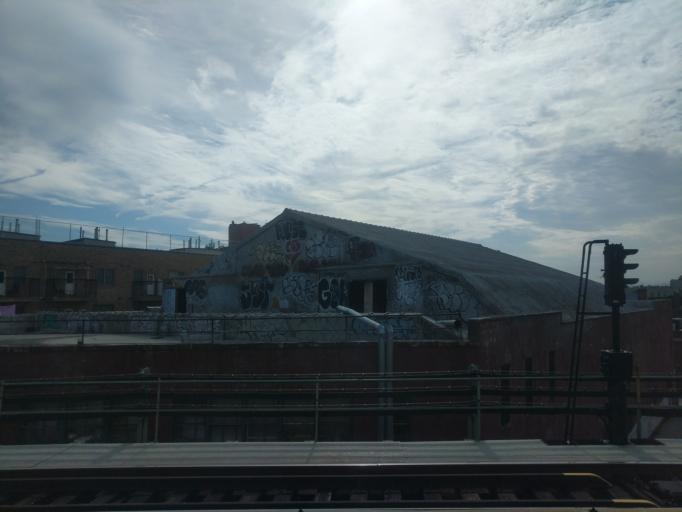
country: US
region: New York
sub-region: Kings County
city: Bensonhurst
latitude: 40.6419
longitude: -73.9944
